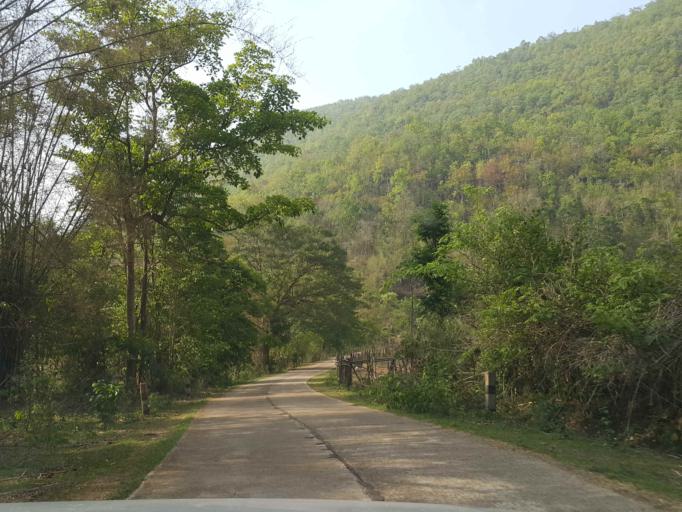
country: TH
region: Chiang Mai
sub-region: Amphoe Chiang Dao
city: Chiang Dao
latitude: 19.3986
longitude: 98.7751
